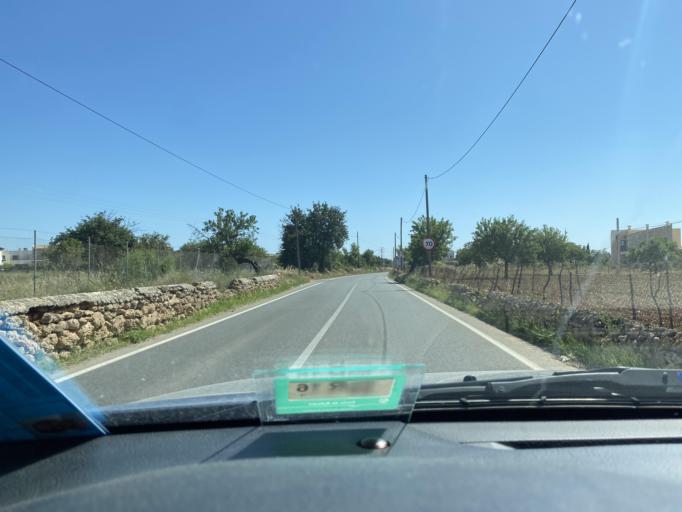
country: ES
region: Balearic Islands
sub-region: Illes Balears
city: Palma
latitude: 39.6157
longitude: 2.6849
